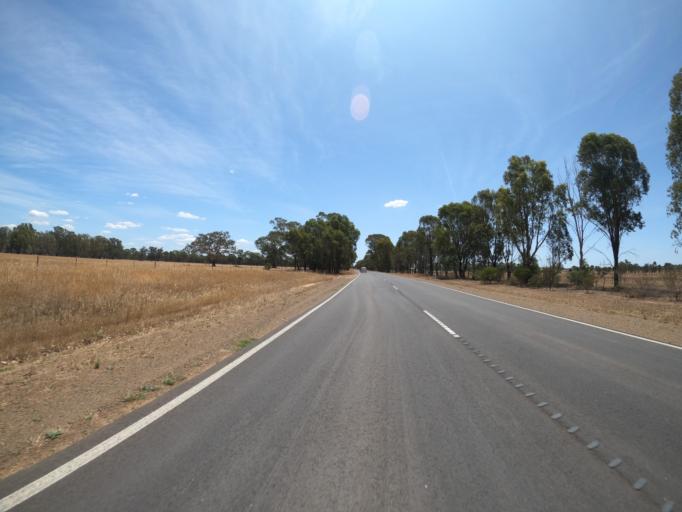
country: AU
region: Victoria
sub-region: Benalla
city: Benalla
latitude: -36.4942
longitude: 146.0181
